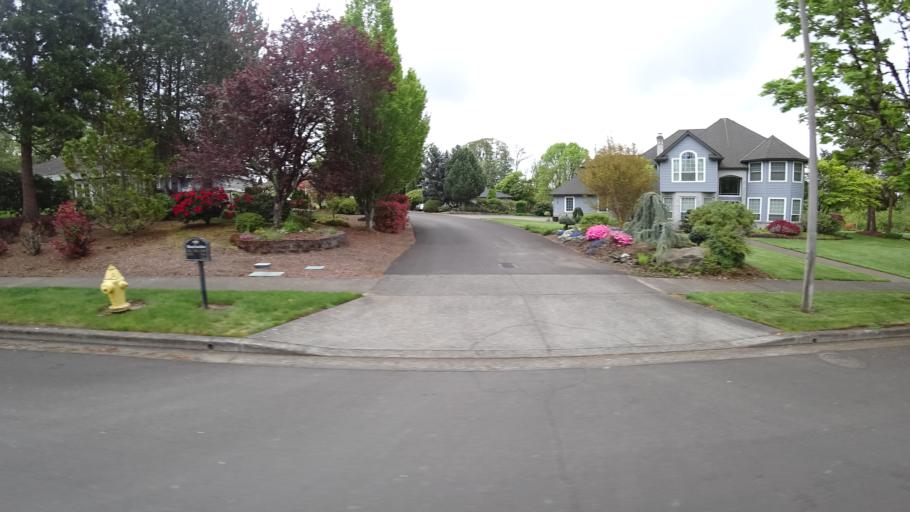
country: US
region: Oregon
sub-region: Washington County
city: Hillsboro
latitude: 45.5481
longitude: -122.9741
